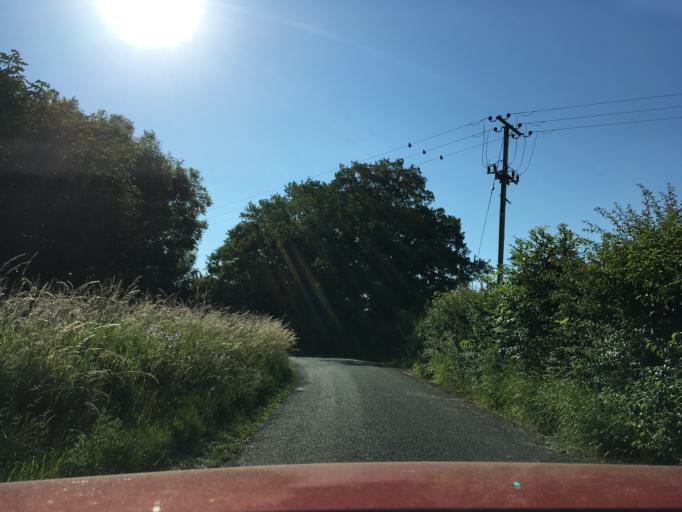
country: GB
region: England
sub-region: South Gloucestershire
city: Hinton
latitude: 51.4775
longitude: -2.3862
